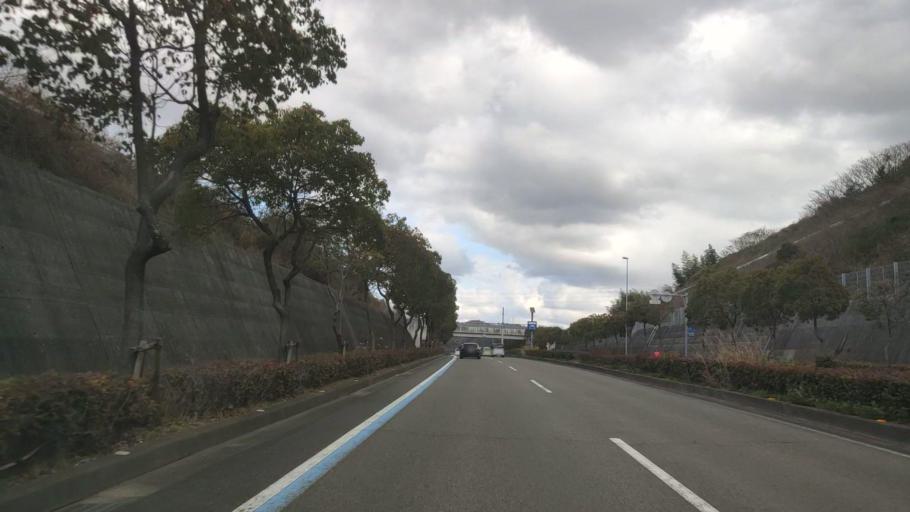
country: JP
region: Ehime
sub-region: Shikoku-chuo Shi
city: Matsuyama
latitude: 33.8897
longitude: 132.7566
